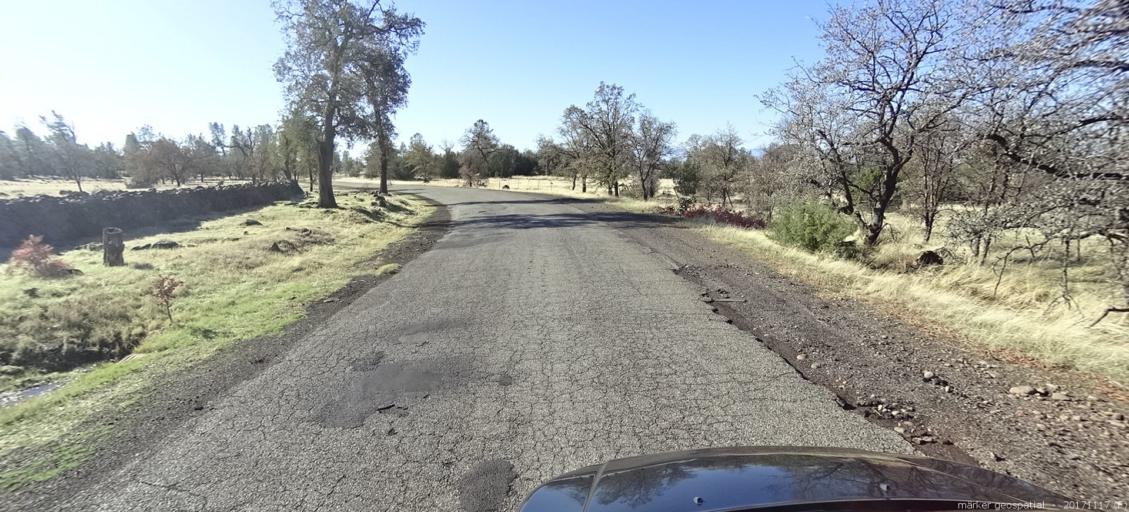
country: US
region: California
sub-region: Shasta County
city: Palo Cedro
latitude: 40.4481
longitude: -122.1146
